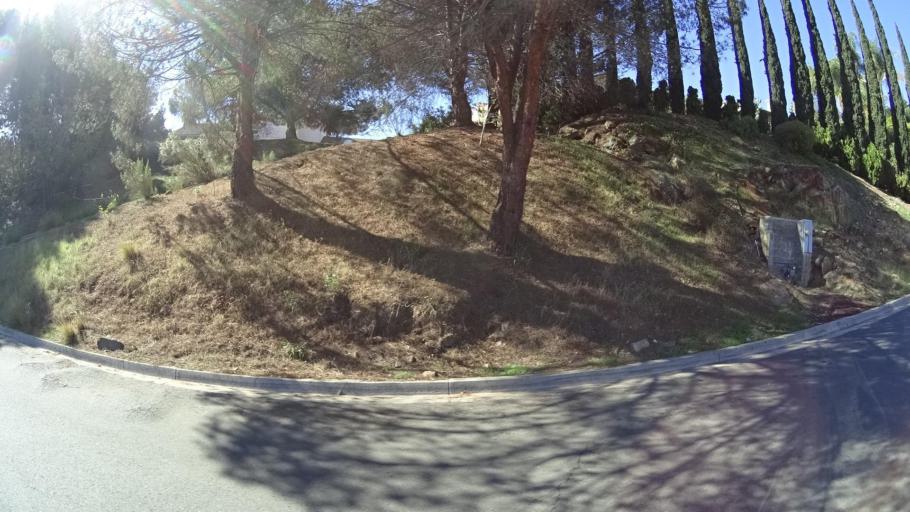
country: US
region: California
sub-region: San Diego County
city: La Presa
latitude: 32.7179
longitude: -116.9821
